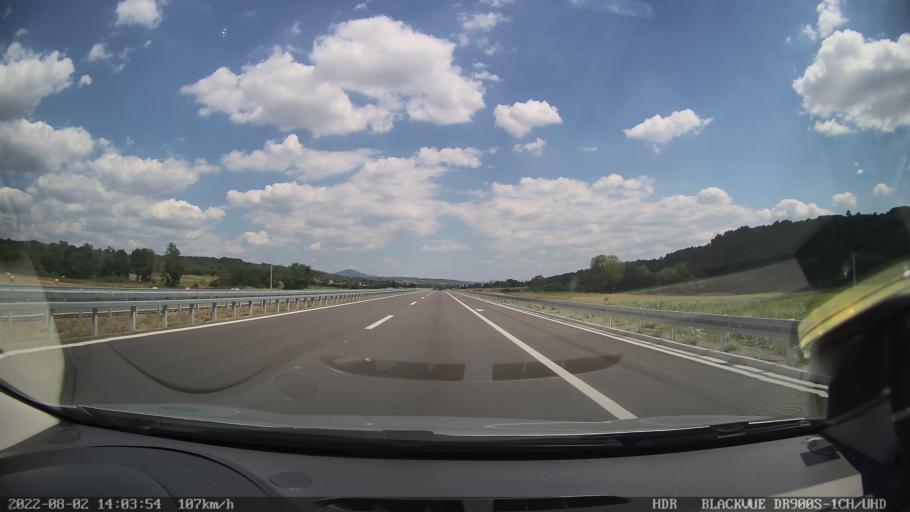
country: RS
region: Central Serbia
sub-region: Moravicki Okrug
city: Cacak
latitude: 43.9243
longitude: 20.3598
